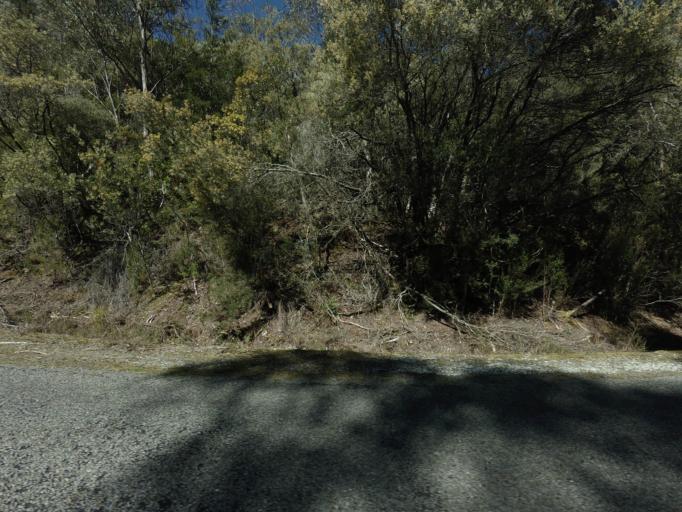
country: AU
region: Tasmania
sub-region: Huon Valley
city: Geeveston
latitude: -42.8113
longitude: 146.3904
